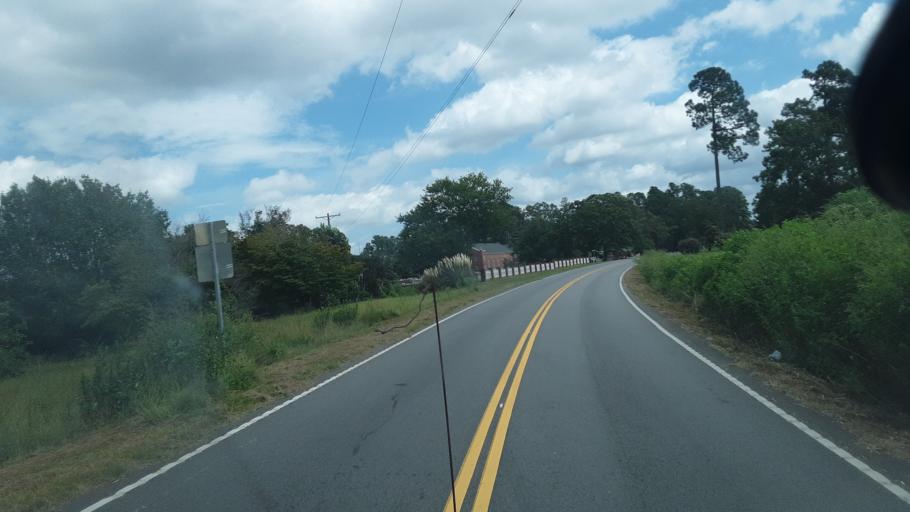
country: US
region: North Carolina
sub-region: Columbus County
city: Tabor City
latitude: 34.2590
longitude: -79.0378
